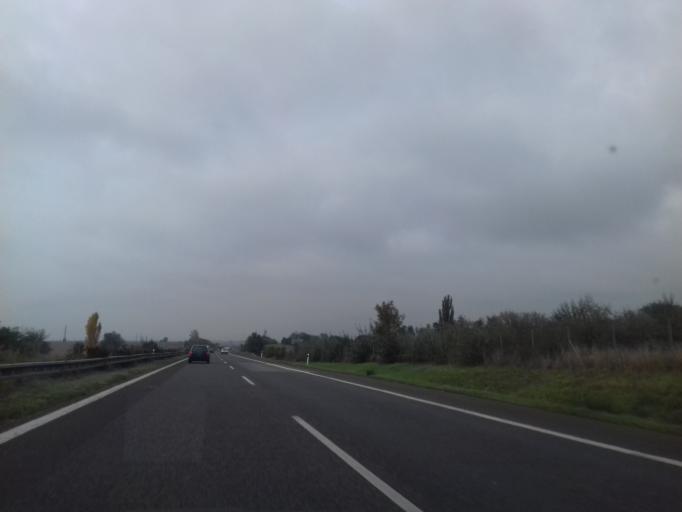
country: SK
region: Bratislavsky
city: Stupava
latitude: 48.2775
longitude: 17.0090
